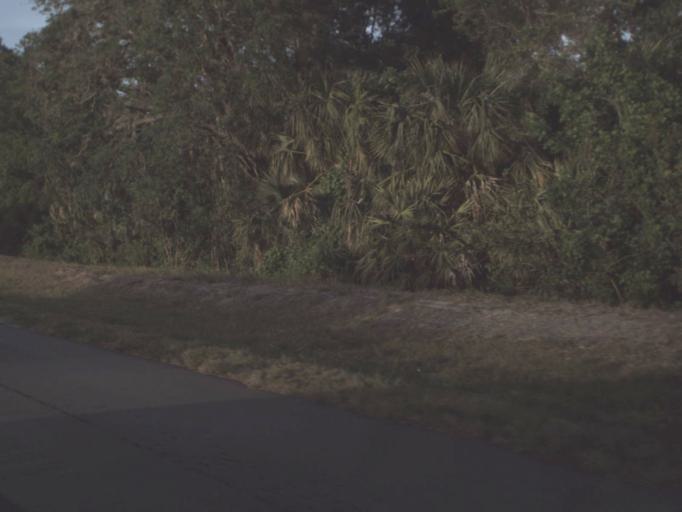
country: US
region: Florida
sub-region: Brevard County
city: Mims
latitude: 28.7195
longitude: -80.8902
